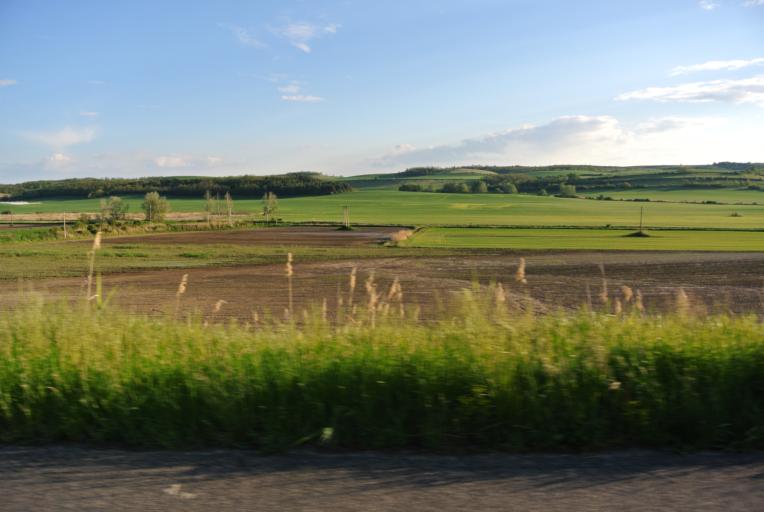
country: HU
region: Komarom-Esztergom
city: Csolnok
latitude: 47.6548
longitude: 18.7104
